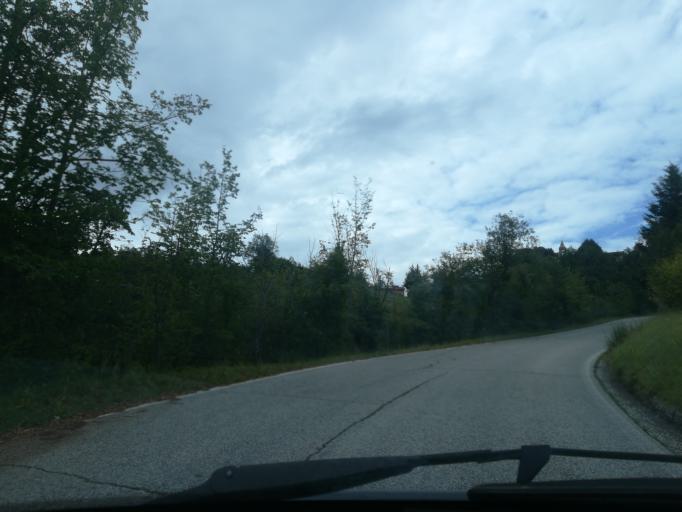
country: IT
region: The Marches
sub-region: Province of Fermo
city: Montefortino
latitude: 42.9385
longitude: 13.3725
